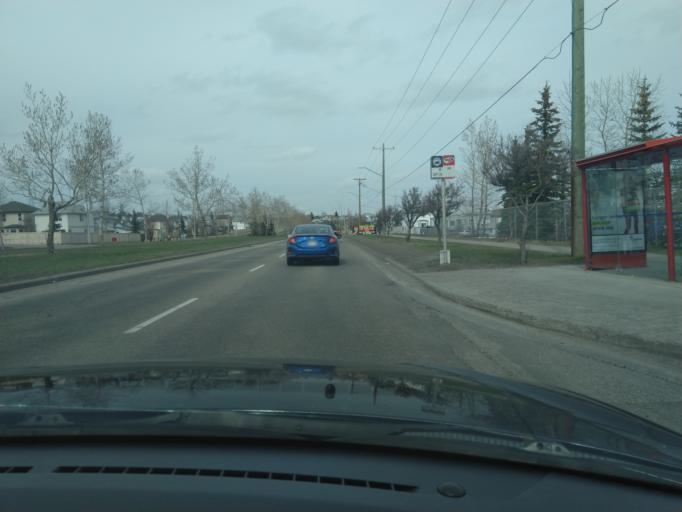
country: CA
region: Alberta
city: Calgary
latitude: 51.1431
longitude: -114.0679
